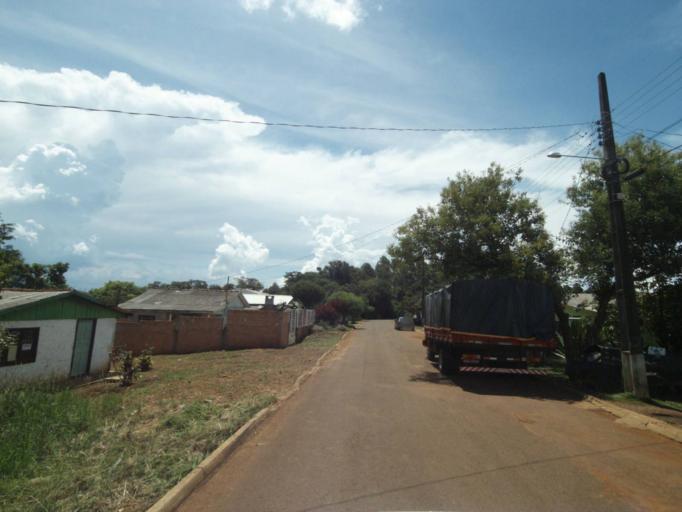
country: BR
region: Parana
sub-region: Guaraniacu
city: Guaraniacu
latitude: -25.0901
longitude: -52.8766
